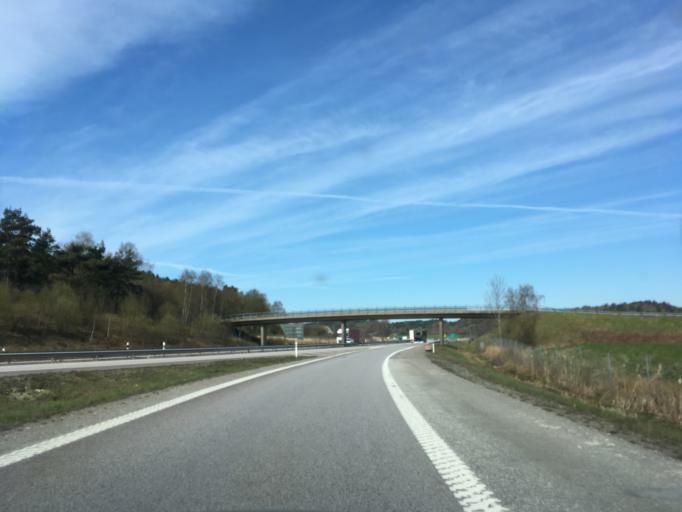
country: SE
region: Halland
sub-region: Kungsbacka Kommun
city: Fjaeras kyrkby
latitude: 57.4327
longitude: 12.1535
